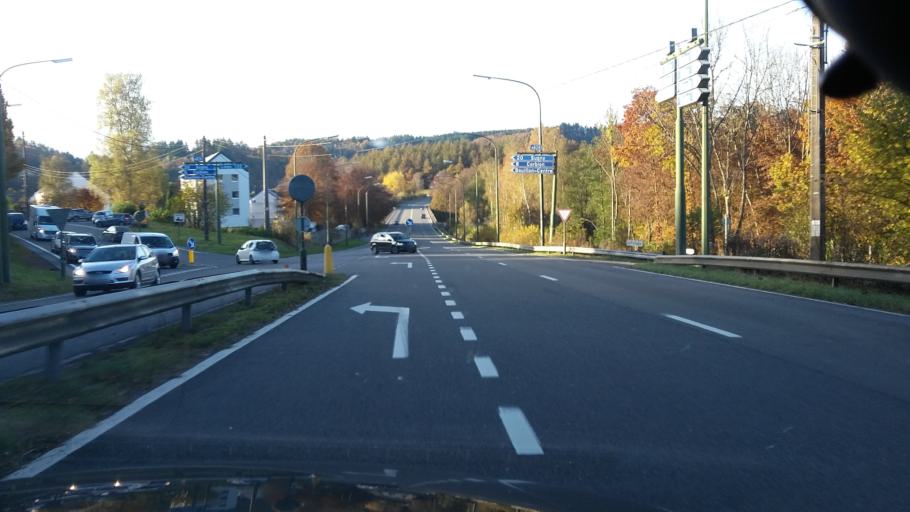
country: BE
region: Wallonia
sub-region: Province du Luxembourg
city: Bouillon
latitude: 49.7835
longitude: 5.0772
